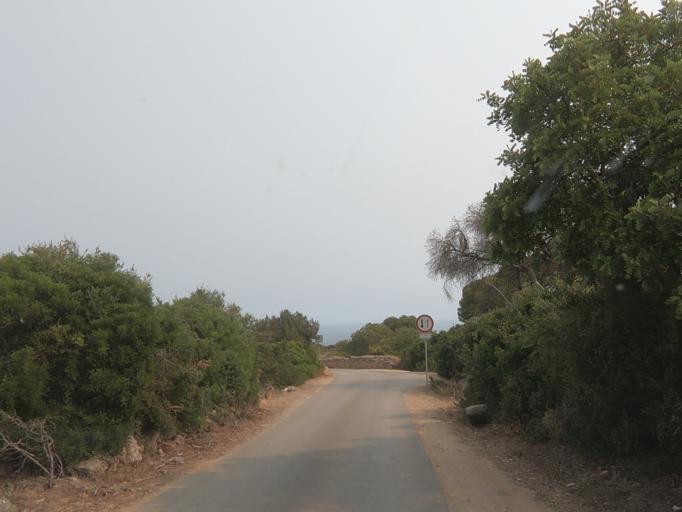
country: PT
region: Faro
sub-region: Lagoa
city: Carvoeiro
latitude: 37.0960
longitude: -8.4069
